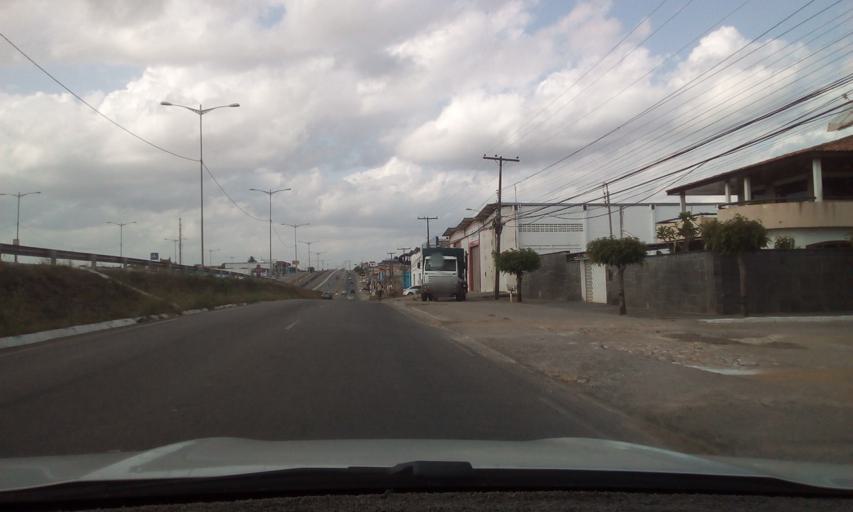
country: BR
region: Pernambuco
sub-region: Caruaru
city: Caruaru
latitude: -8.2609
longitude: -35.9758
